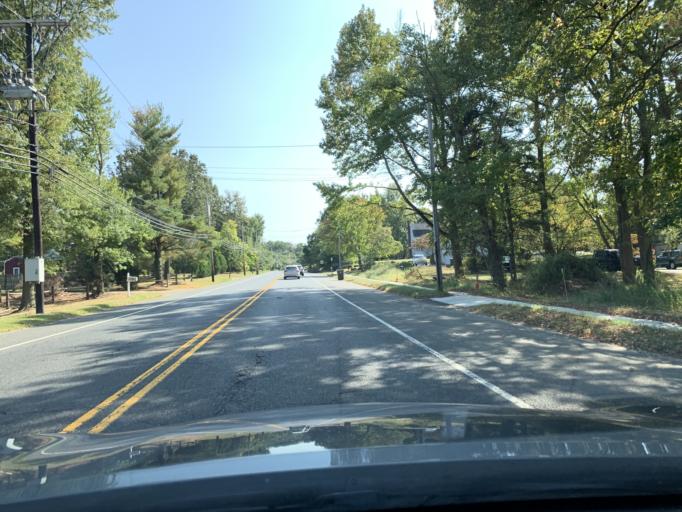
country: US
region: New Jersey
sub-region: Monmouth County
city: Tinton Falls
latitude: 40.2962
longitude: -74.0952
